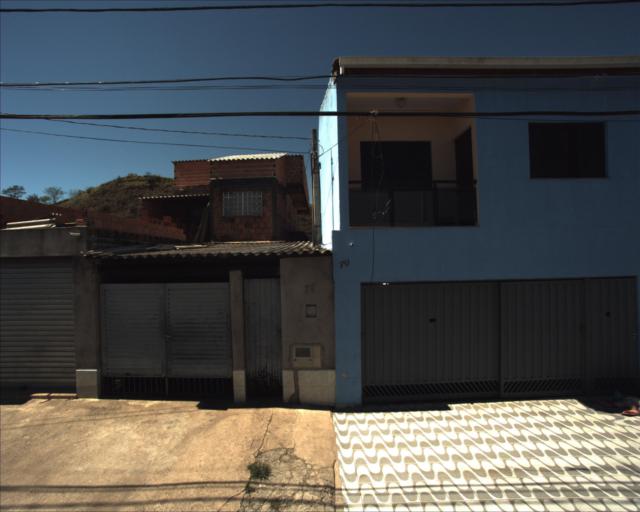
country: BR
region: Sao Paulo
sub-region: Votorantim
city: Votorantim
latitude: -23.5237
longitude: -47.4344
